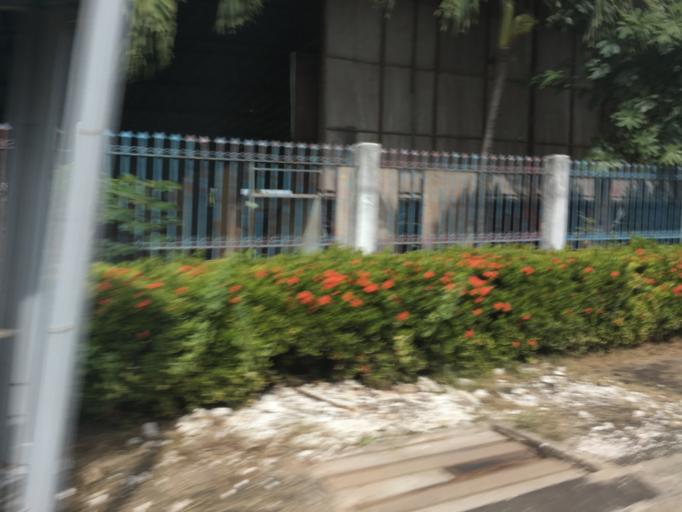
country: TH
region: Chachoengsao
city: Bang Khla
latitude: 13.7337
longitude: 101.2121
